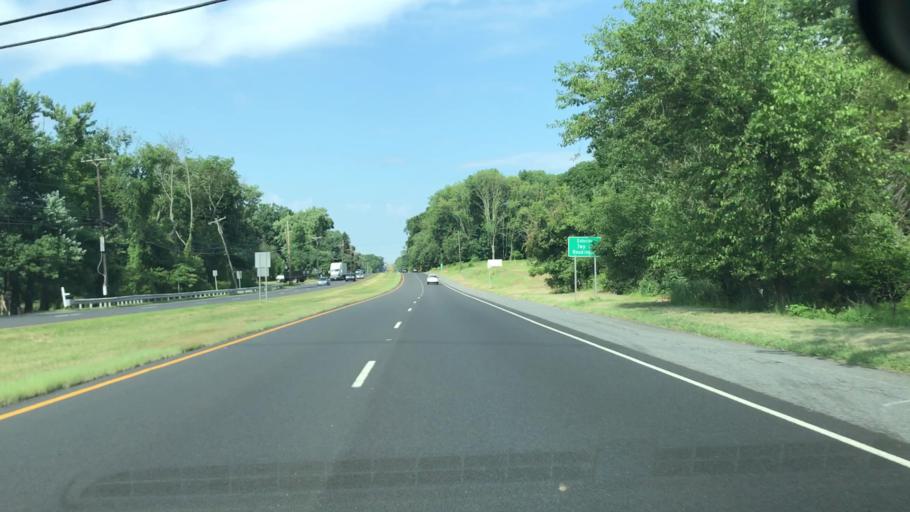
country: US
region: New Jersey
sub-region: Hunterdon County
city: Whitehouse Station
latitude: 40.5446
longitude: -74.7485
